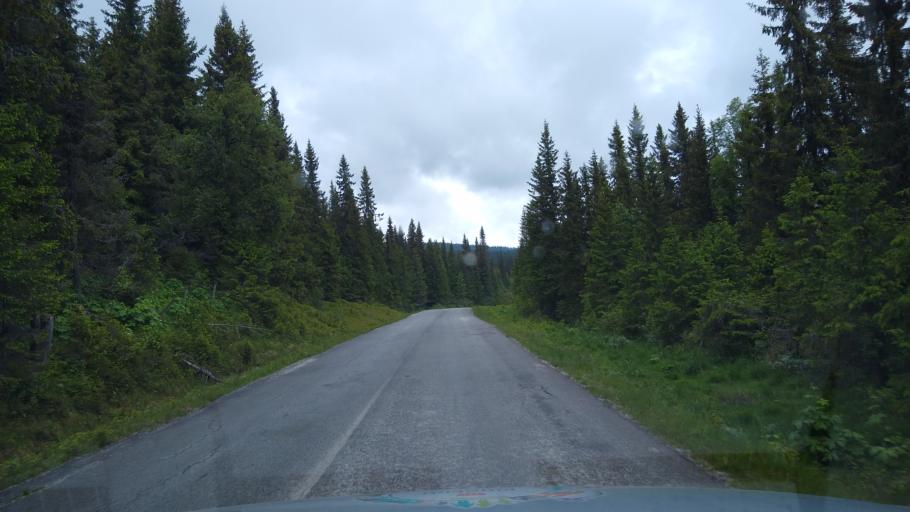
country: NO
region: Oppland
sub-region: Ringebu
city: Ringebu
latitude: 61.4867
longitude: 10.1151
